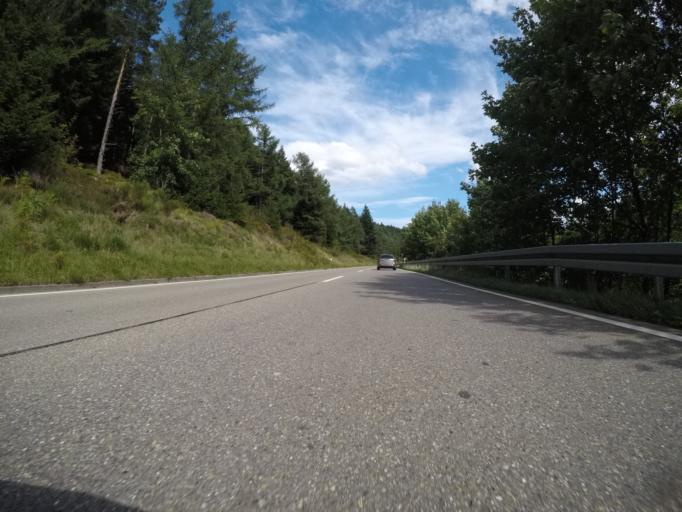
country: DE
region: Baden-Wuerttemberg
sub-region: Karlsruhe Region
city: Baiersbronn
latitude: 48.4622
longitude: 8.3619
